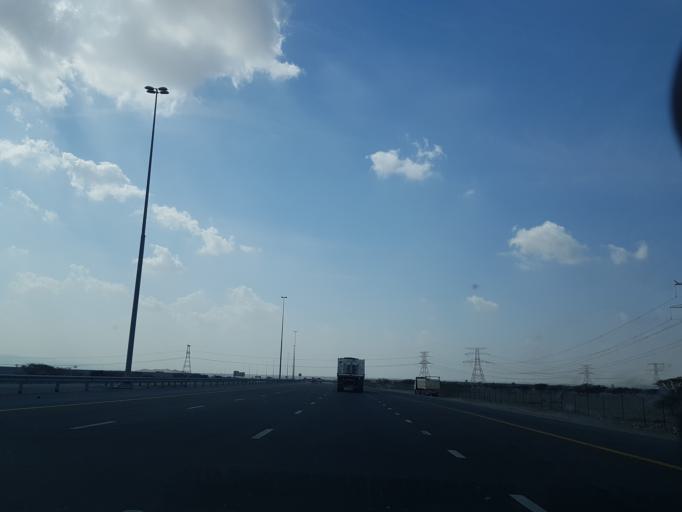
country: AE
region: Ra's al Khaymah
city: Ras al-Khaimah
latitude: 25.7571
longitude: 56.0191
